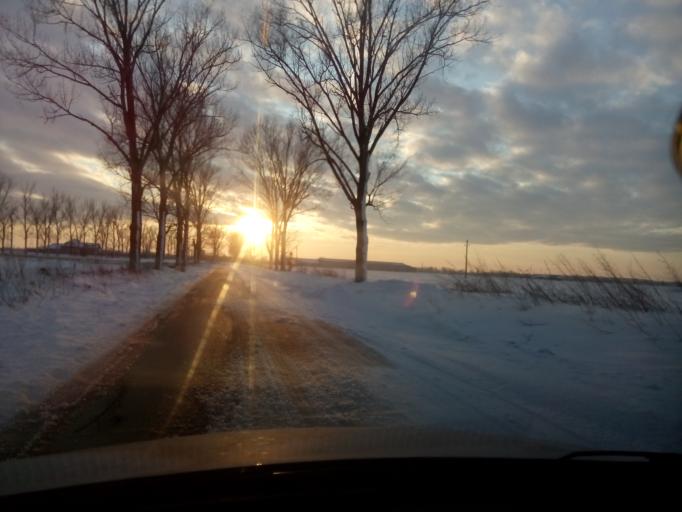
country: RO
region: Calarasi
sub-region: Comuna Luica
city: Luica
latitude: 44.2357
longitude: 26.5985
